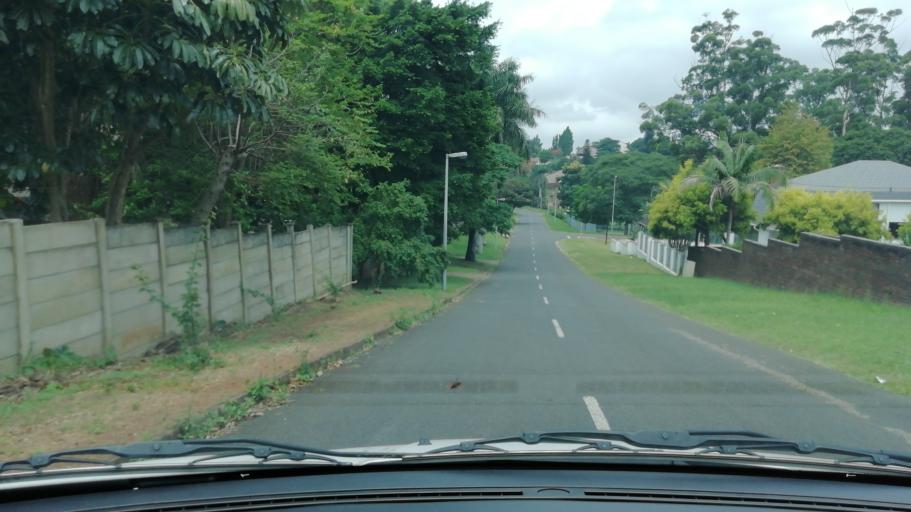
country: ZA
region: KwaZulu-Natal
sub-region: uThungulu District Municipality
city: Empangeni
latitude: -28.7486
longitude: 31.8870
